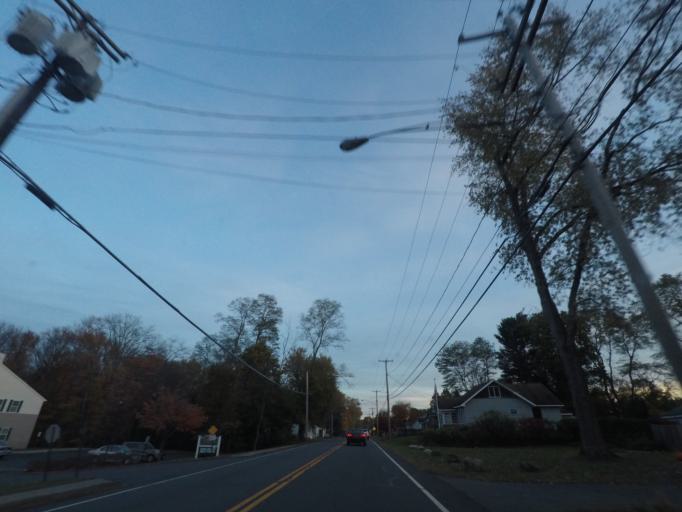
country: US
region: New York
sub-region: Schenectady County
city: Rotterdam
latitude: 42.7682
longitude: -73.9432
